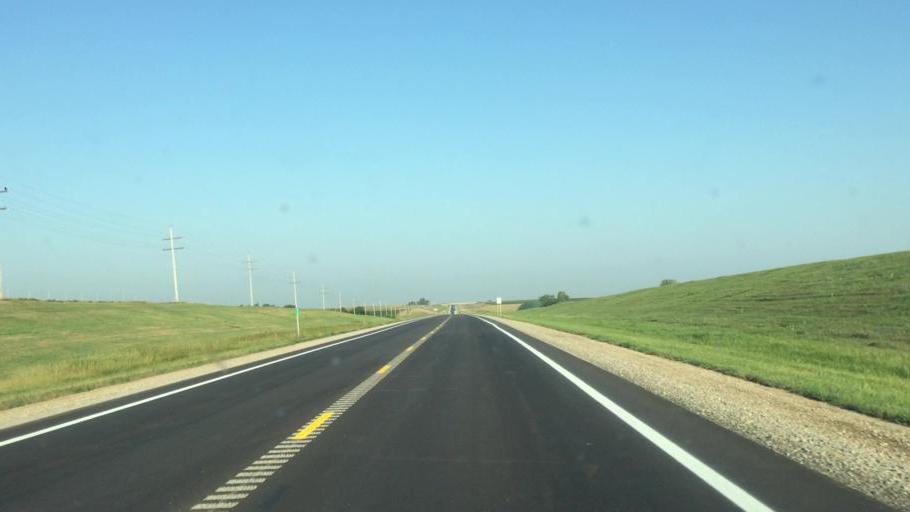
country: US
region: Kansas
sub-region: Brown County
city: Hiawatha
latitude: 39.8421
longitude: -95.4258
